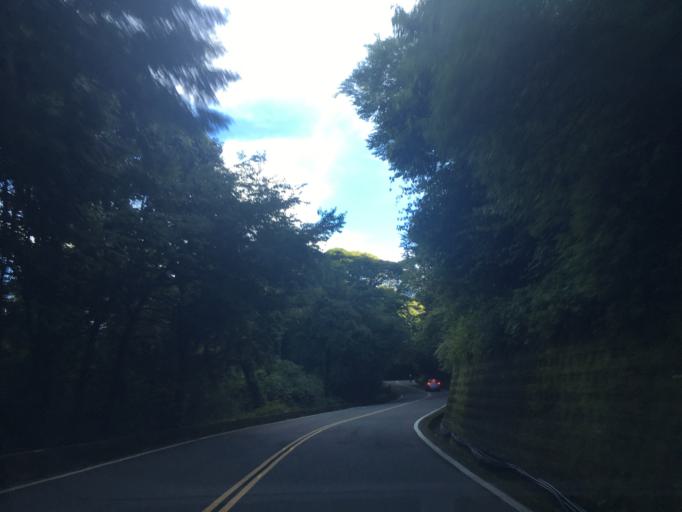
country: TW
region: Taiwan
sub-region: Nantou
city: Puli
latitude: 24.0859
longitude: 121.1714
